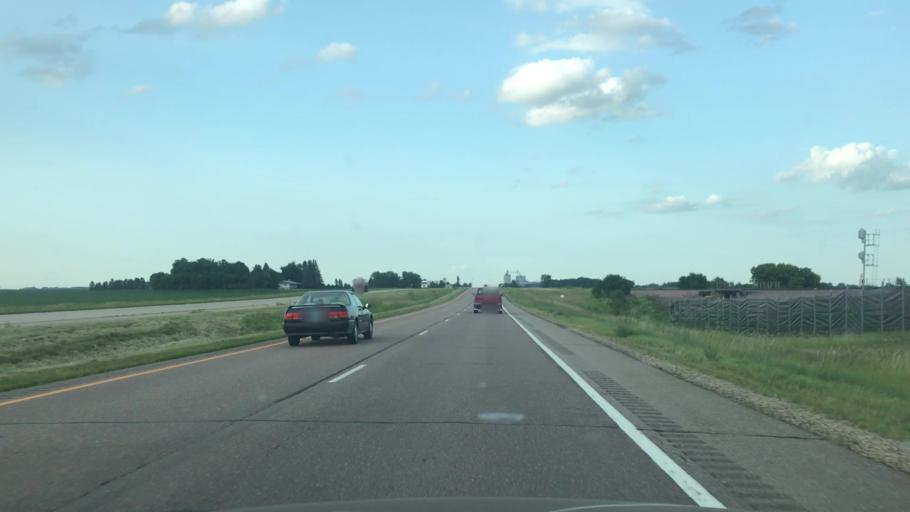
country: US
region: Minnesota
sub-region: Nobles County
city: Worthington
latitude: 43.6804
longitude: -95.4995
